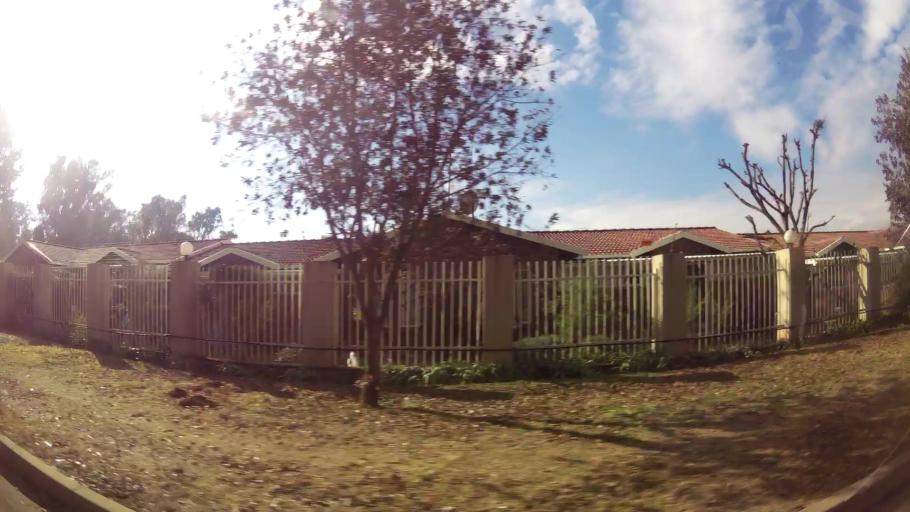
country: ZA
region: Gauteng
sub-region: Sedibeng District Municipality
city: Meyerton
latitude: -26.5482
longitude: 28.0610
